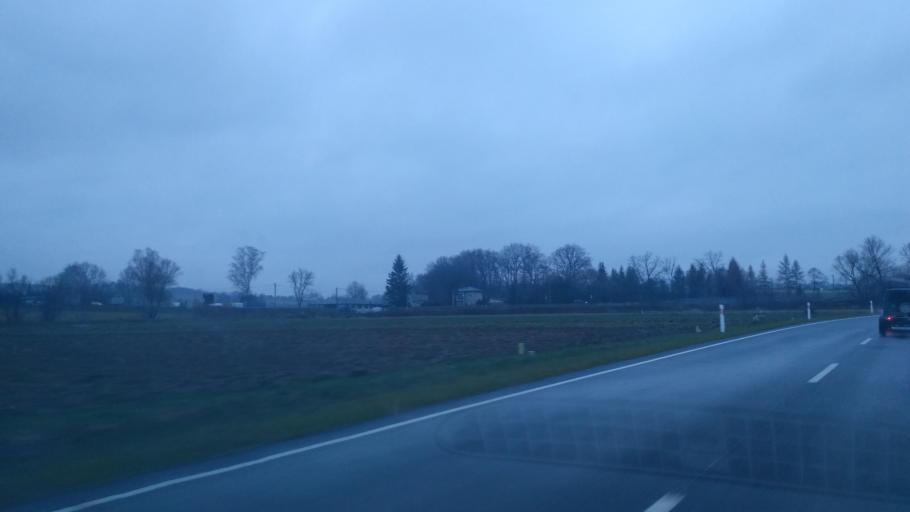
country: PL
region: Subcarpathian Voivodeship
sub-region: Powiat rzeszowski
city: Dynow
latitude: 49.8321
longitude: 22.2418
